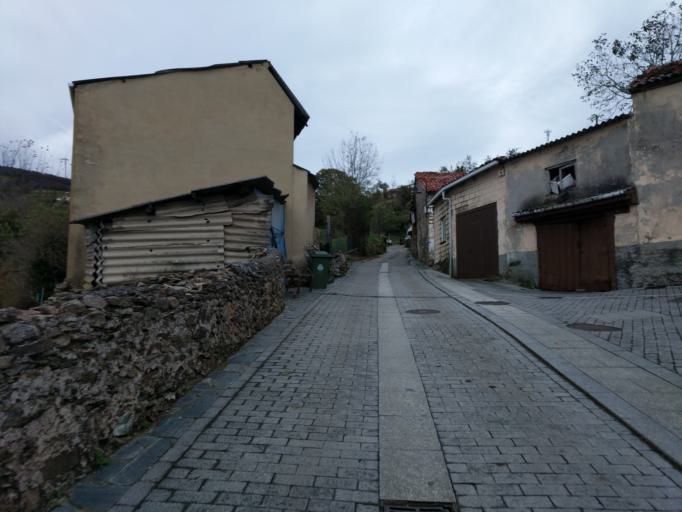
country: ES
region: Asturias
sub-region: Province of Asturias
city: Tineo
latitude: 43.3364
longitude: -6.4139
